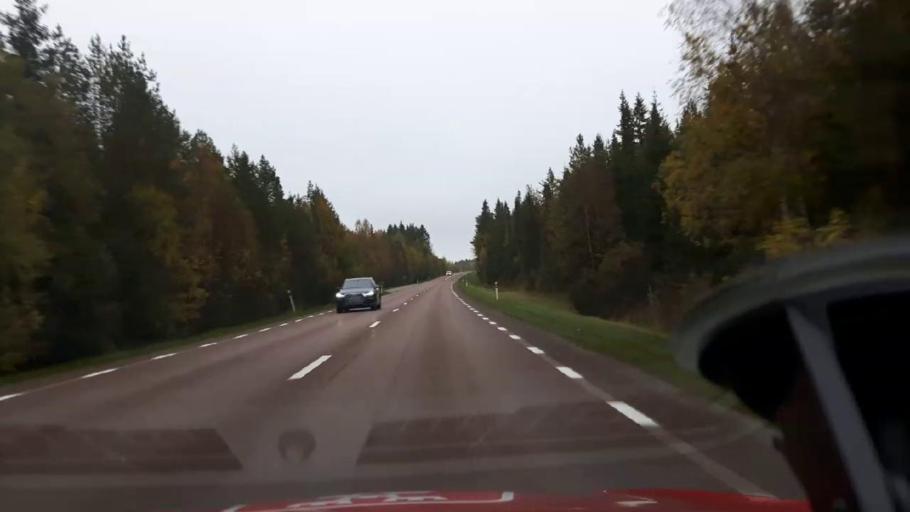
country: SE
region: Jaemtland
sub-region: Bergs Kommun
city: Hoverberg
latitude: 62.5905
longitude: 14.4311
